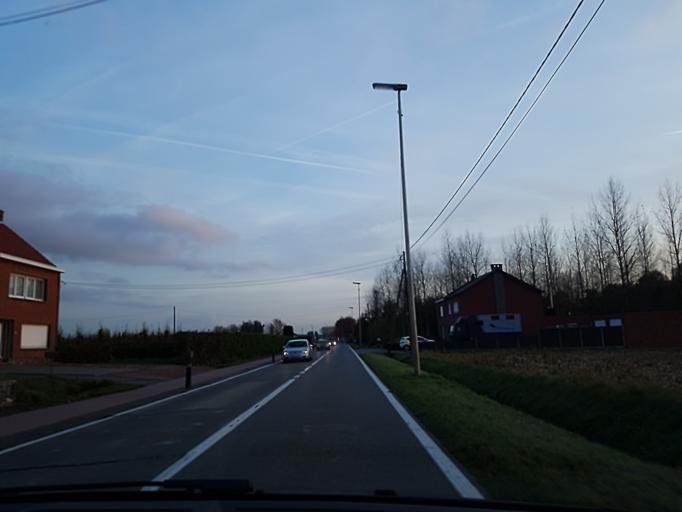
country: BE
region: Flanders
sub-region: Provincie Antwerpen
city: Ranst
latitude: 51.1694
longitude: 4.5641
